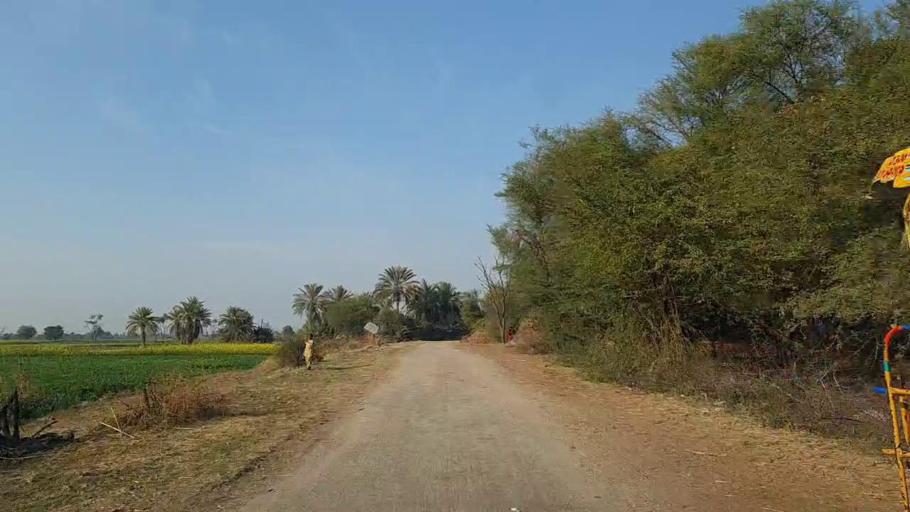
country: PK
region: Sindh
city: Nawabshah
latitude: 26.3681
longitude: 68.4907
